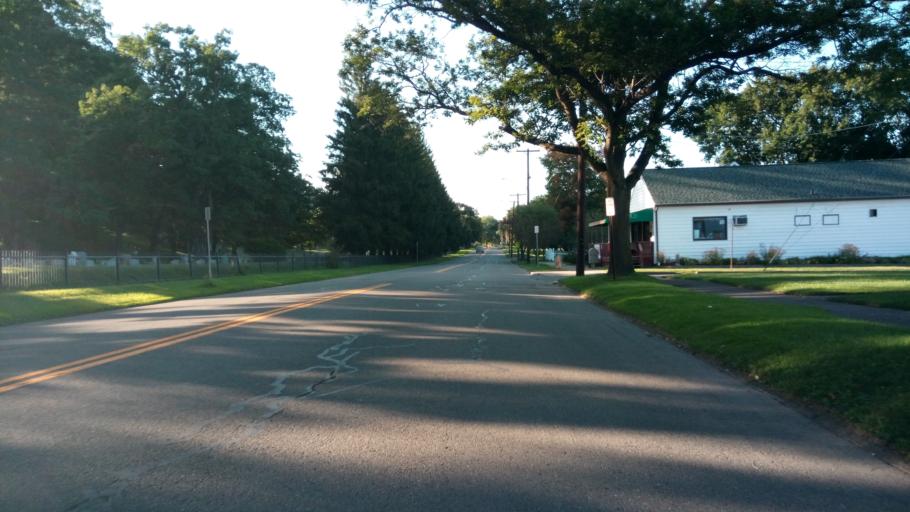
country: US
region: New York
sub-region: Chemung County
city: Elmira
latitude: 42.1058
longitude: -76.8237
